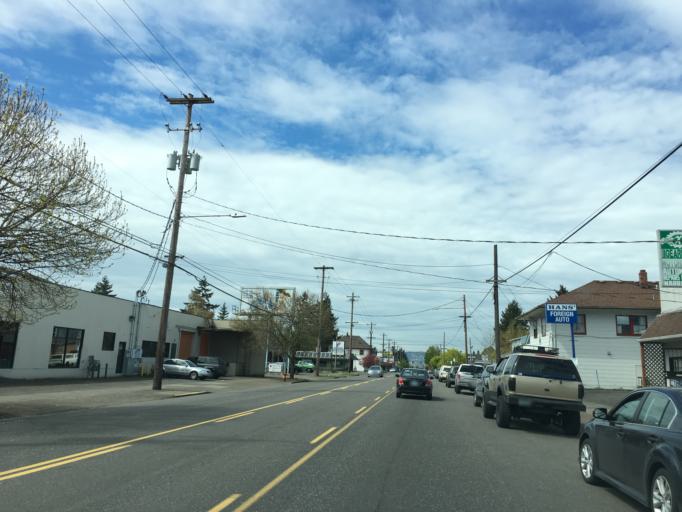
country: US
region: Oregon
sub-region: Multnomah County
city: Lents
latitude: 45.5265
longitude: -122.5900
